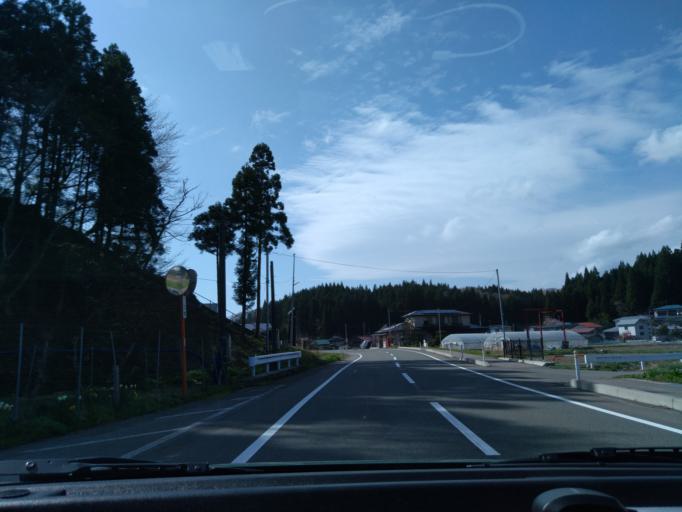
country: JP
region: Akita
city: Akita
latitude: 39.7134
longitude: 140.1994
